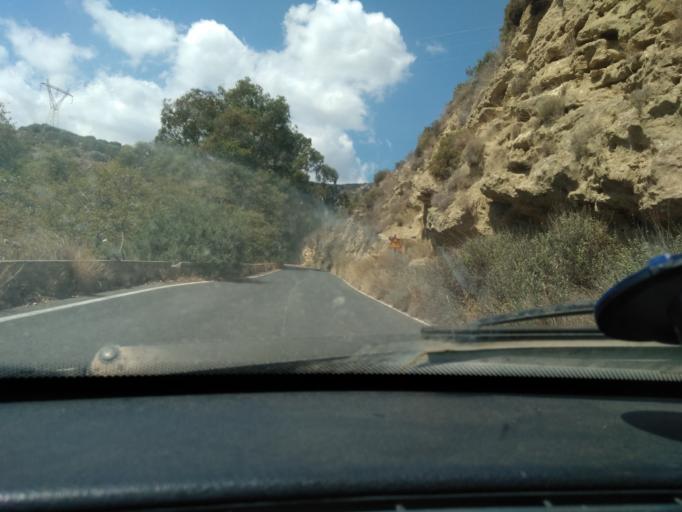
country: GR
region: Crete
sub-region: Nomos Lasithiou
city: Siteia
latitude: 35.1406
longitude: 26.0740
